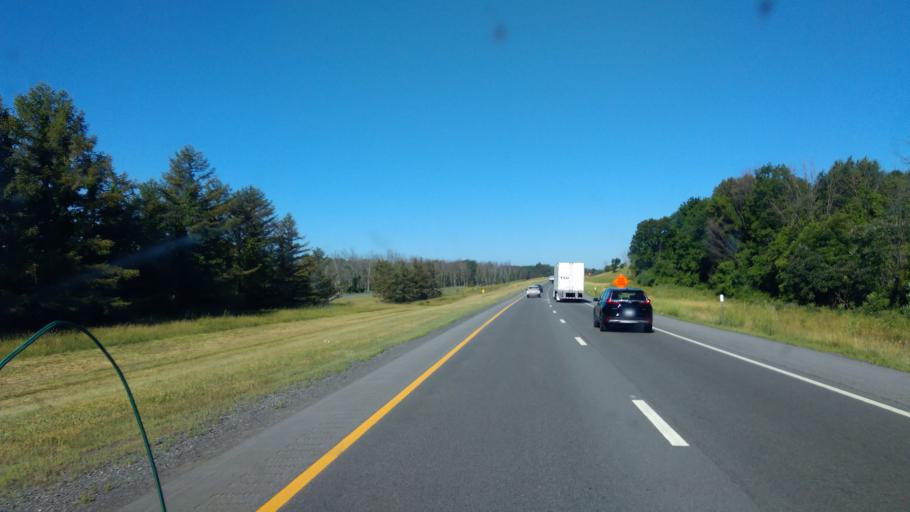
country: US
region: New York
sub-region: Livingston County
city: Caledonia
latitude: 43.0312
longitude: -77.8295
